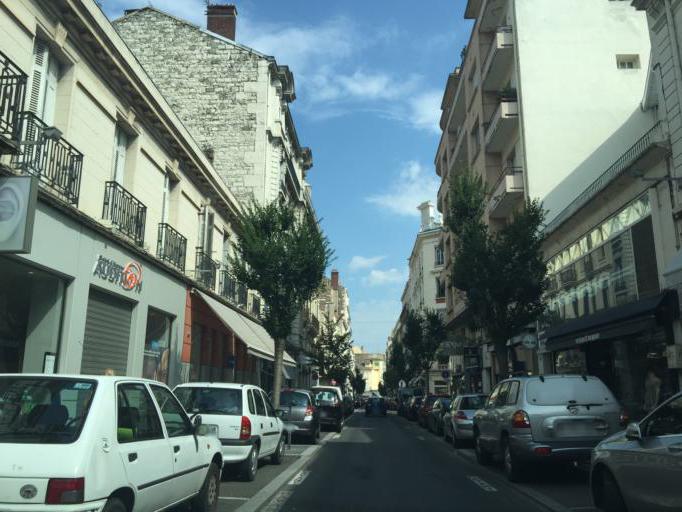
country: FR
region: Rhone-Alpes
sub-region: Departement de la Loire
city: Saint-Etienne
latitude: 45.4349
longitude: 4.3896
